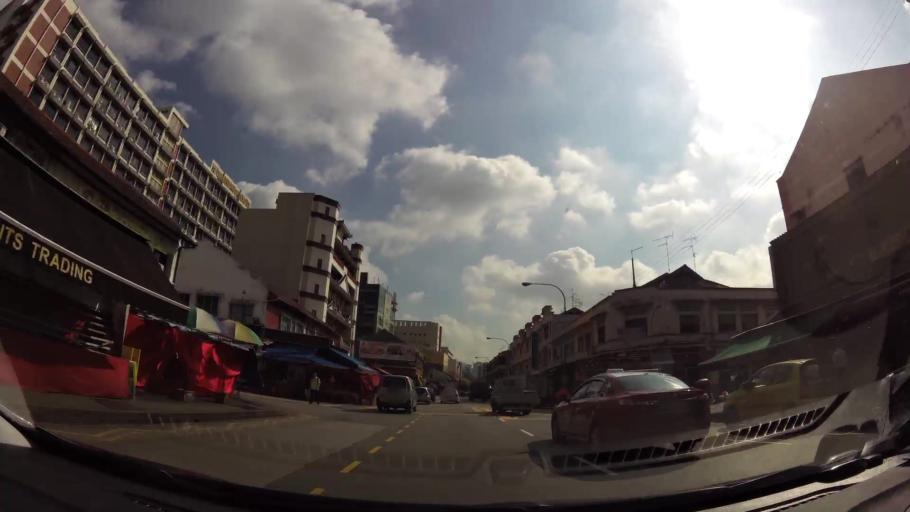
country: SG
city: Singapore
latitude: 1.3139
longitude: 103.8771
